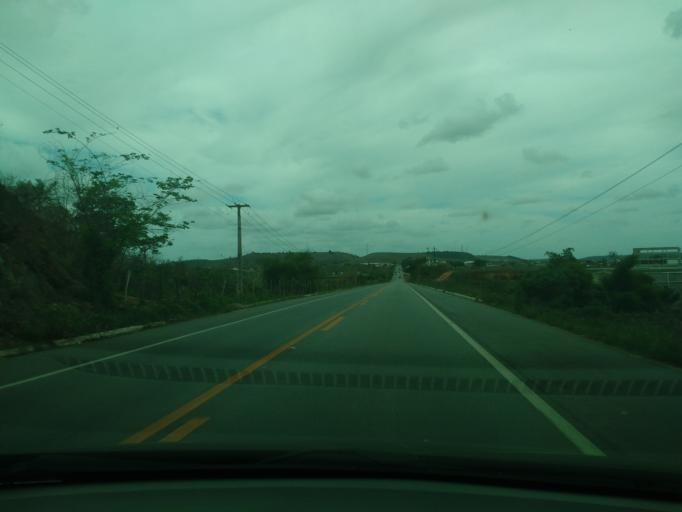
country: BR
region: Alagoas
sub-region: Murici
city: Murici
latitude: -9.3013
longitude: -35.9519
